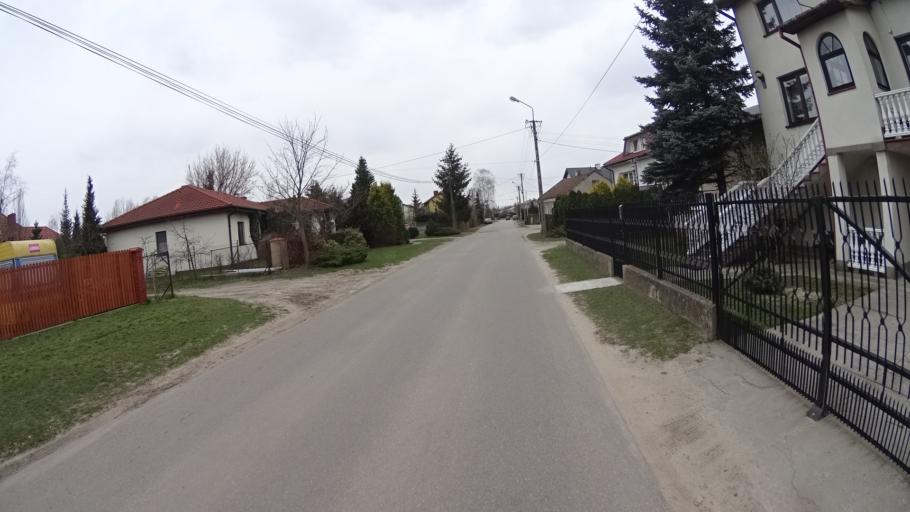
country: PL
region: Masovian Voivodeship
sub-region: Powiat warszawski zachodni
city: Truskaw
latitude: 52.2601
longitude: 20.7498
